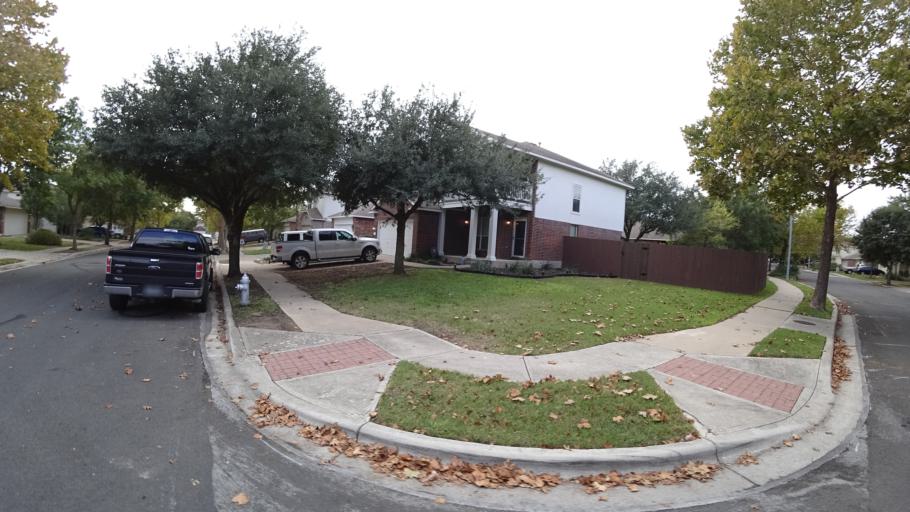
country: US
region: Texas
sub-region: Travis County
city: Manchaca
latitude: 30.1550
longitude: -97.8392
